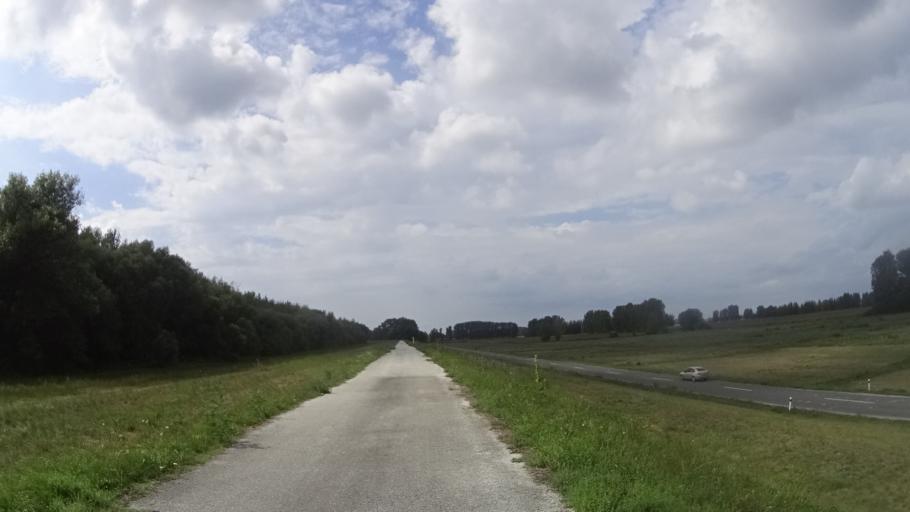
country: SK
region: Trnavsky
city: Gabcikovo
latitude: 47.8051
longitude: 17.6447
